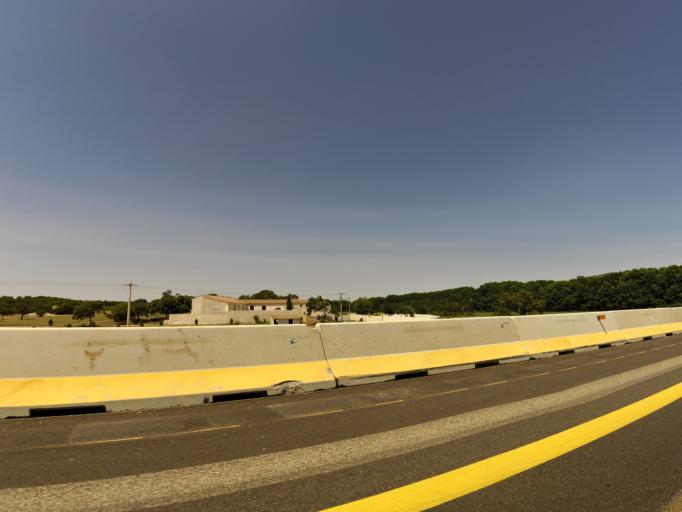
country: FR
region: Languedoc-Roussillon
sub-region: Departement de l'Herault
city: Baillargues
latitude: 43.6736
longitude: 4.0188
